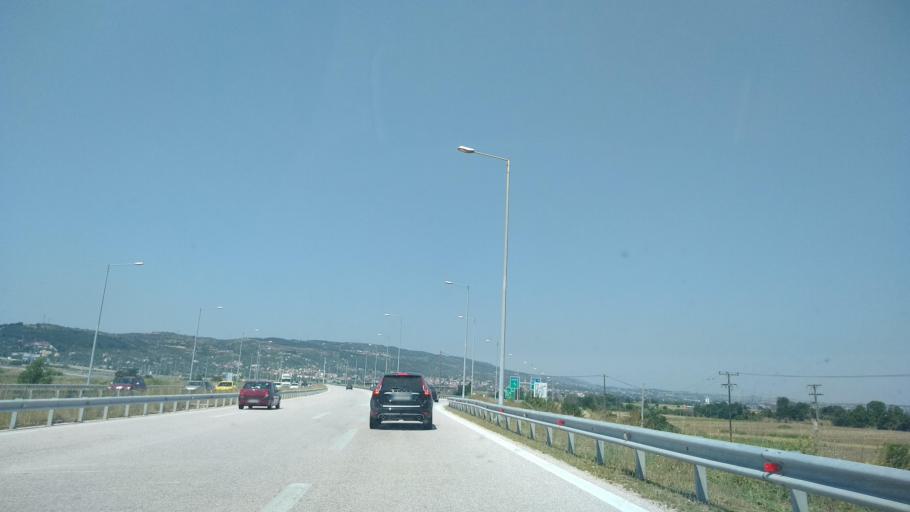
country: GR
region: Central Macedonia
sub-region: Nomos Thessalonikis
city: Lagyna
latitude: 40.7394
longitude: 23.0187
